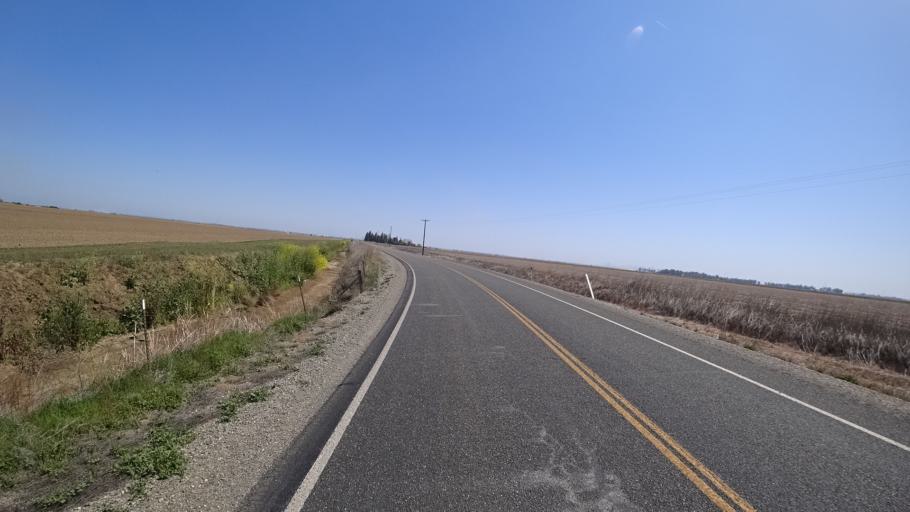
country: US
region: California
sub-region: Glenn County
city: Willows
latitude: 39.4648
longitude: -122.1354
